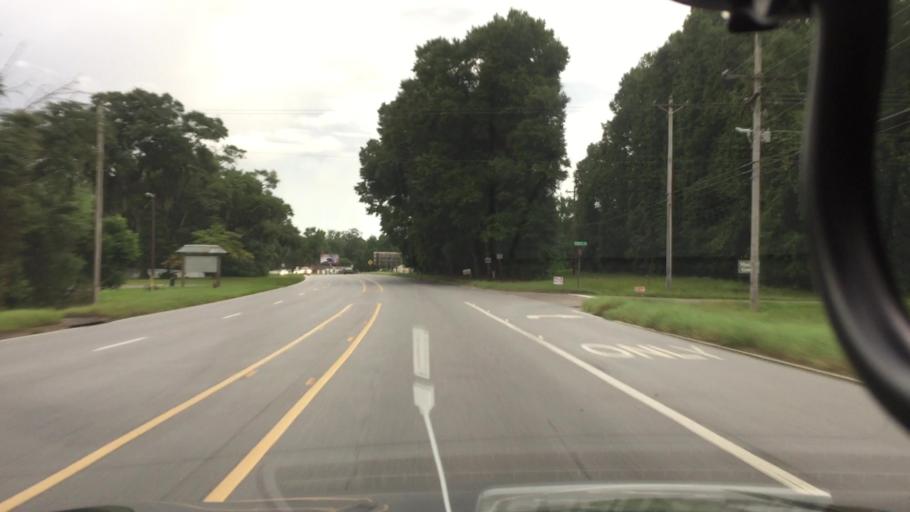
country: US
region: Alabama
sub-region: Pike County
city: Troy
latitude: 31.7583
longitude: -85.9613
